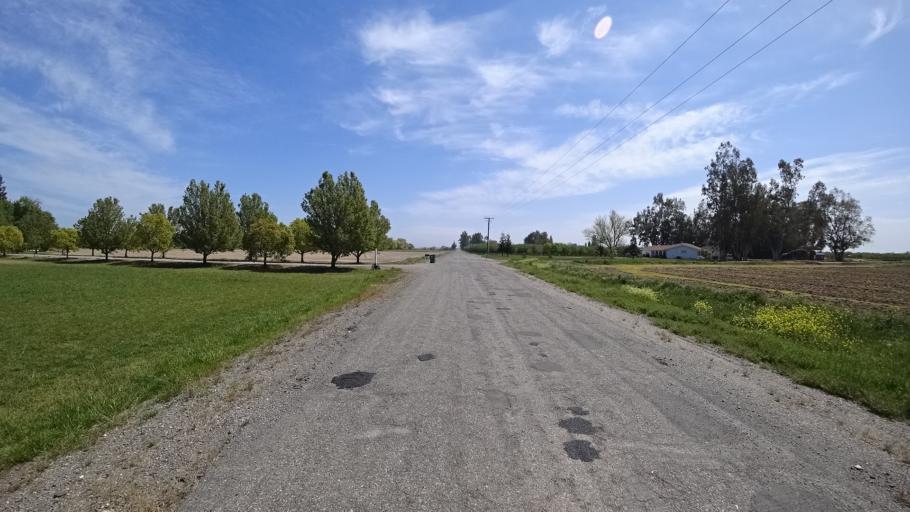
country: US
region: California
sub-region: Glenn County
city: Hamilton City
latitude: 39.6017
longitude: -122.0620
